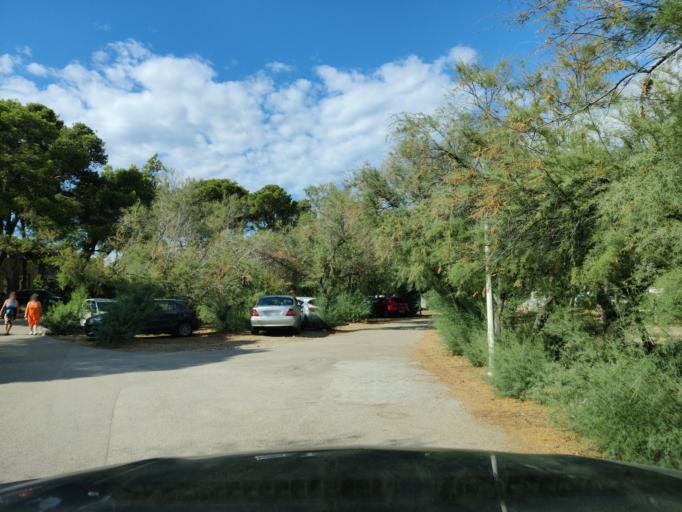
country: HR
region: Sibensko-Kniniska
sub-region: Grad Sibenik
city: Sibenik
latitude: 43.7247
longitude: 15.8473
